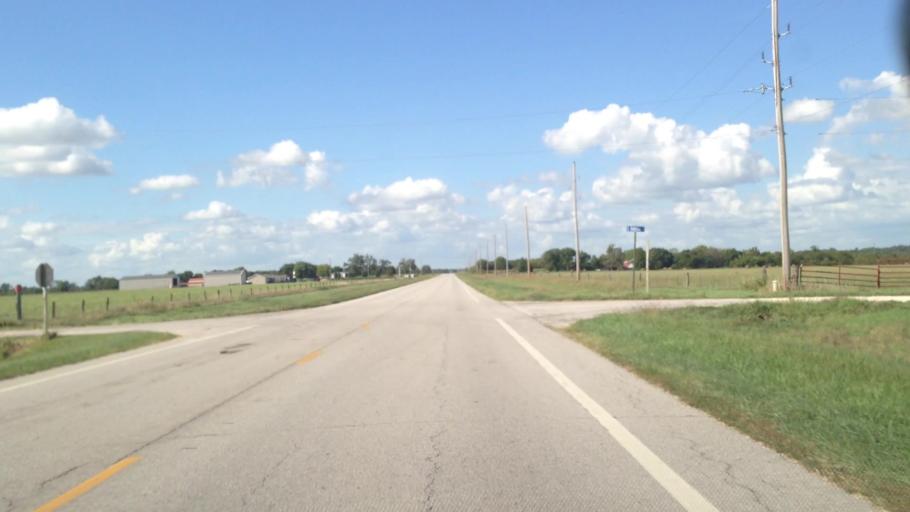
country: US
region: Kansas
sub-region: Allen County
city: Iola
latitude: 37.9786
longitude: -95.1713
